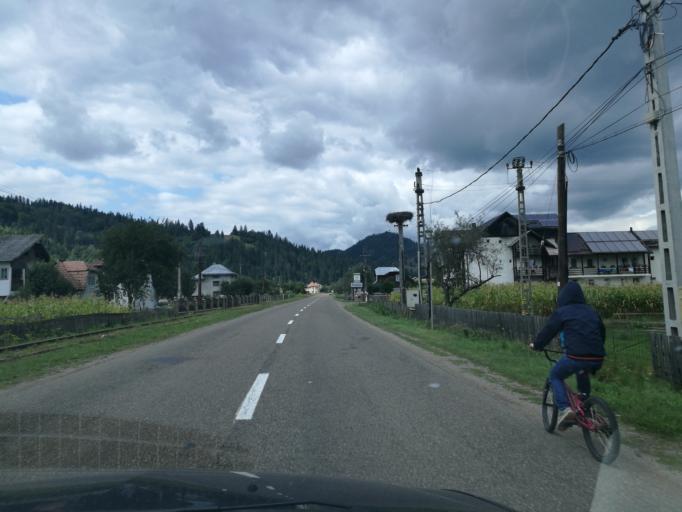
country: RO
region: Suceava
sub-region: Comuna Frumosu
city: Frumosu
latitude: 47.5978
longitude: 25.6595
